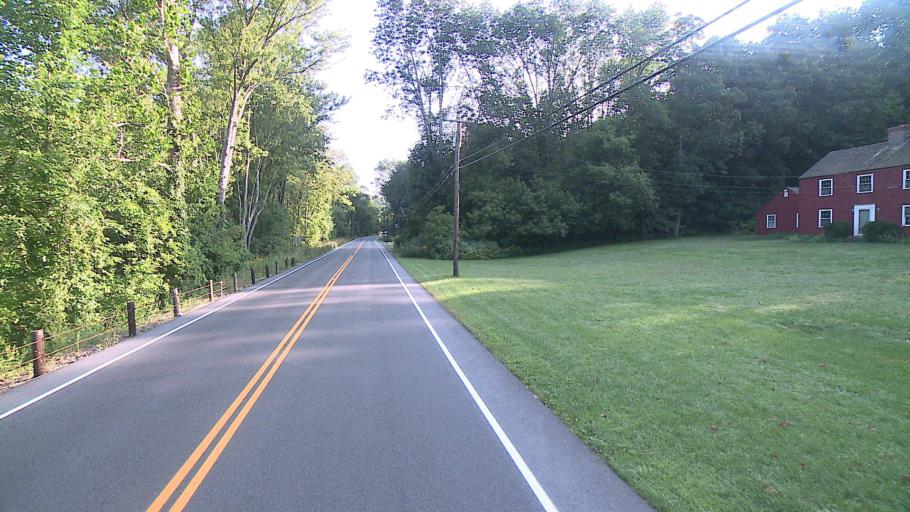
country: US
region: Connecticut
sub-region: Litchfield County
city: Kent
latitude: 41.6872
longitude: -73.5056
